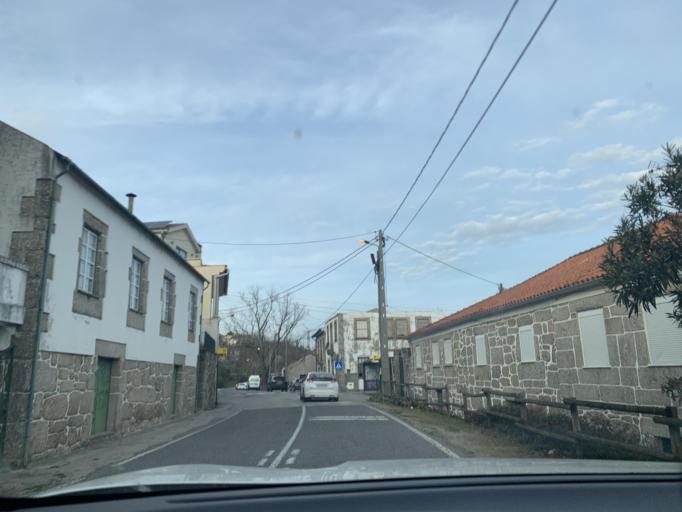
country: PT
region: Viseu
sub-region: Viseu
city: Viseu
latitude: 40.6065
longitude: -7.9794
